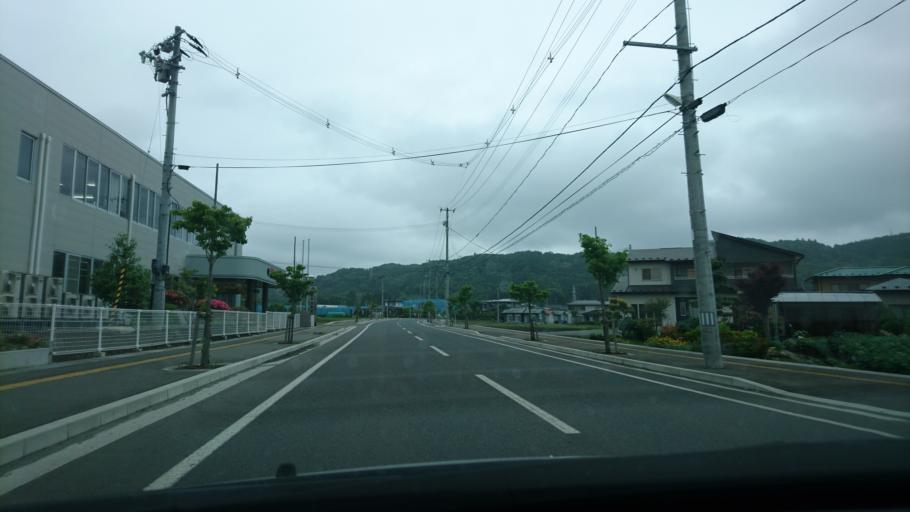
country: JP
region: Iwate
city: Ichinoseki
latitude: 38.9379
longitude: 141.0837
